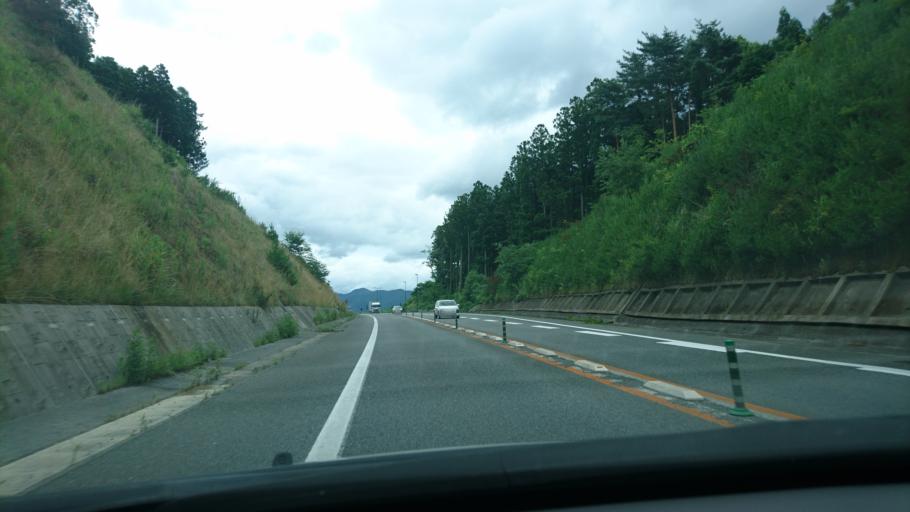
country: JP
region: Iwate
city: Ofunato
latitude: 39.0299
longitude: 141.7082
